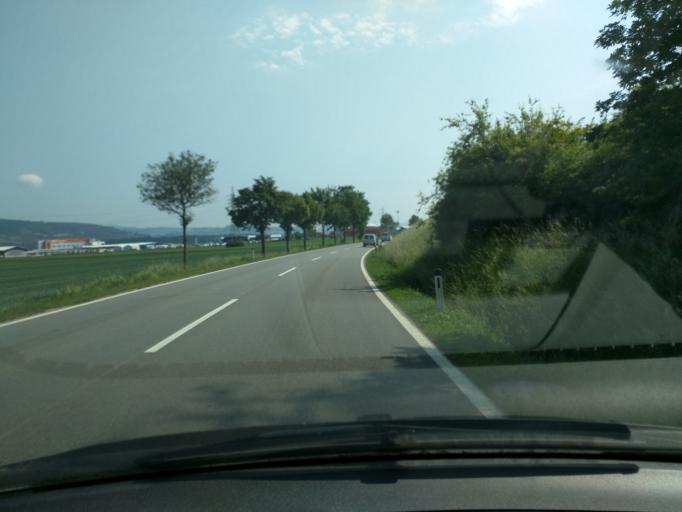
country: AT
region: Lower Austria
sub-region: Politischer Bezirk Melk
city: Pochlarn
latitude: 48.1971
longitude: 15.2165
